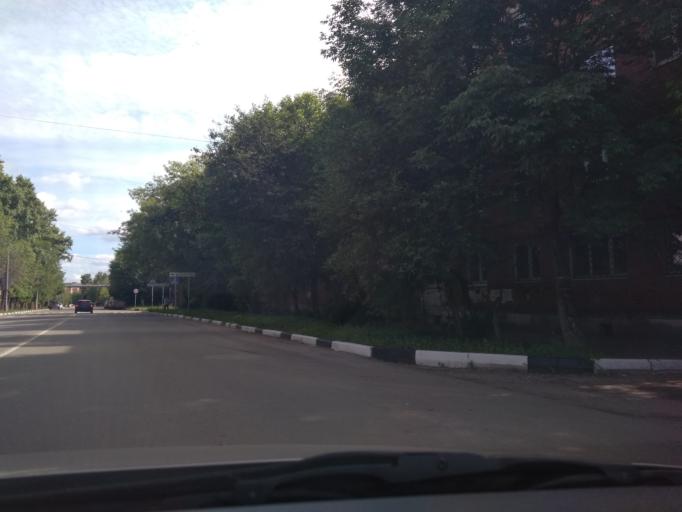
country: RU
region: Moskovskaya
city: Orekhovo-Zuyevo
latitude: 55.8128
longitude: 38.9677
